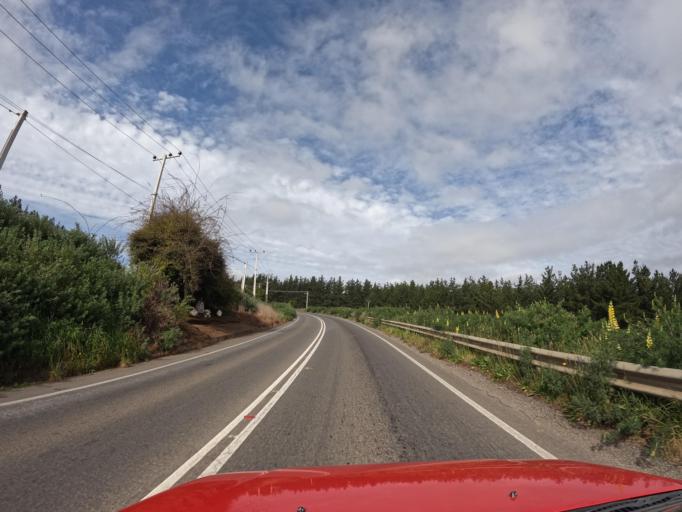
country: CL
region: O'Higgins
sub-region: Provincia de Colchagua
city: Santa Cruz
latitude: -34.3683
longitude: -71.9578
